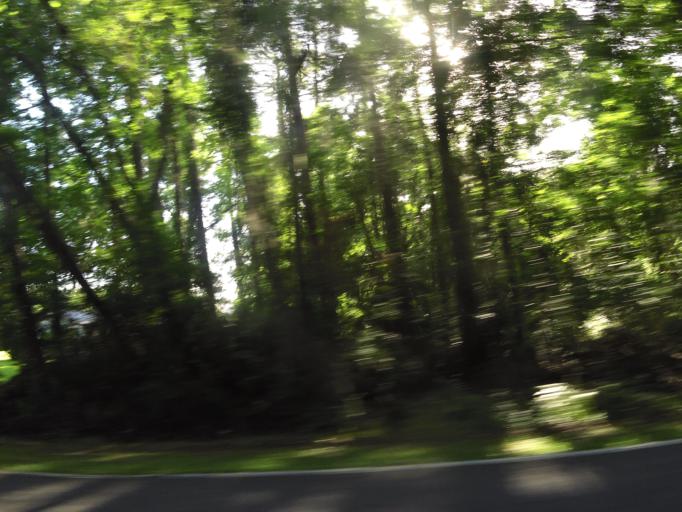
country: US
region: Florida
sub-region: Nassau County
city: Nassau Village-Ratliff
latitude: 30.4749
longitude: -81.7846
